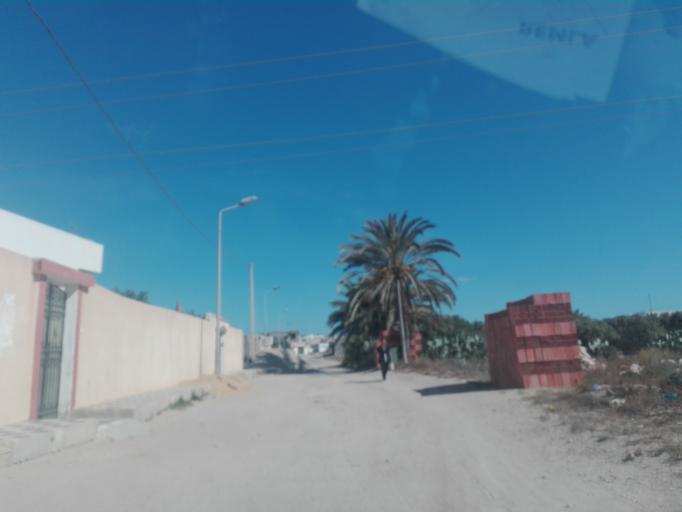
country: TN
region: Safaqis
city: Al Qarmadah
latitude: 34.7085
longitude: 11.1995
